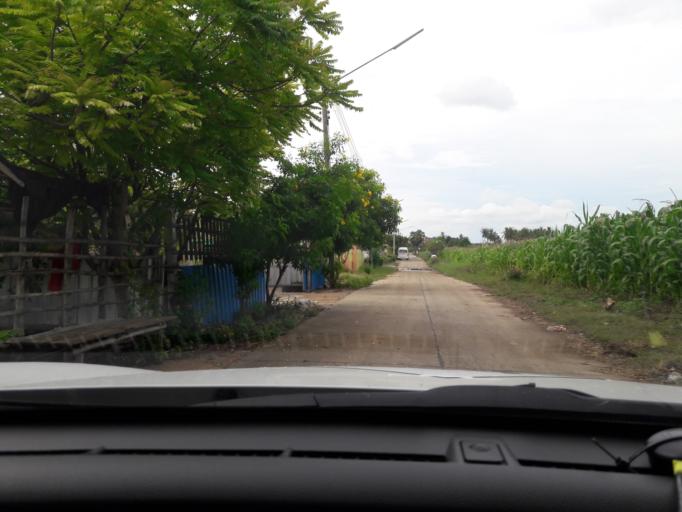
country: TH
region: Nakhon Sawan
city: Tak Fa
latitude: 15.3426
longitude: 100.5032
